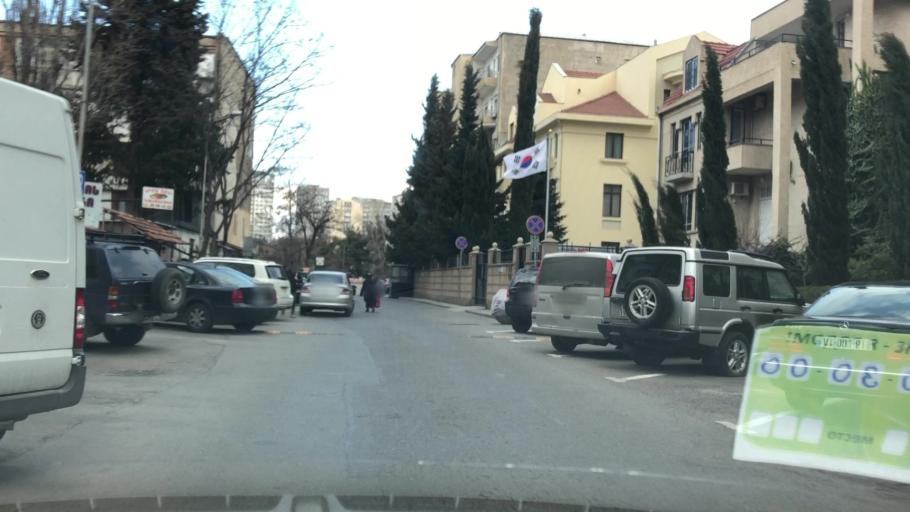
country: GE
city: Tsqnet'i
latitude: 41.7125
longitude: 44.7612
